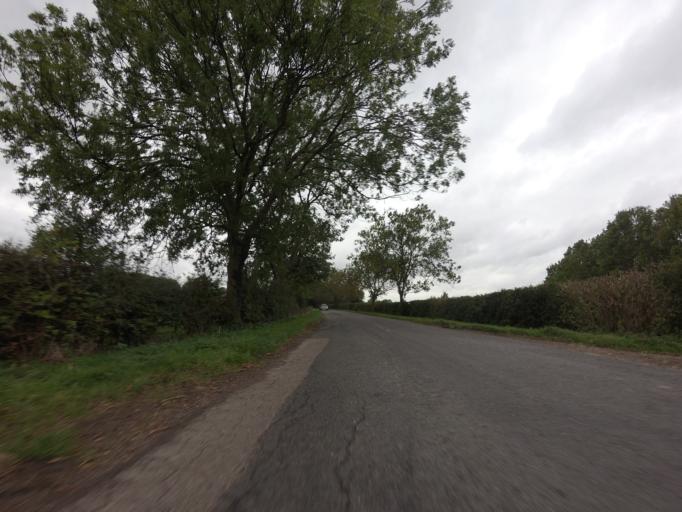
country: GB
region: England
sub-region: Cambridgeshire
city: Haslingfield
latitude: 52.1537
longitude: 0.0367
